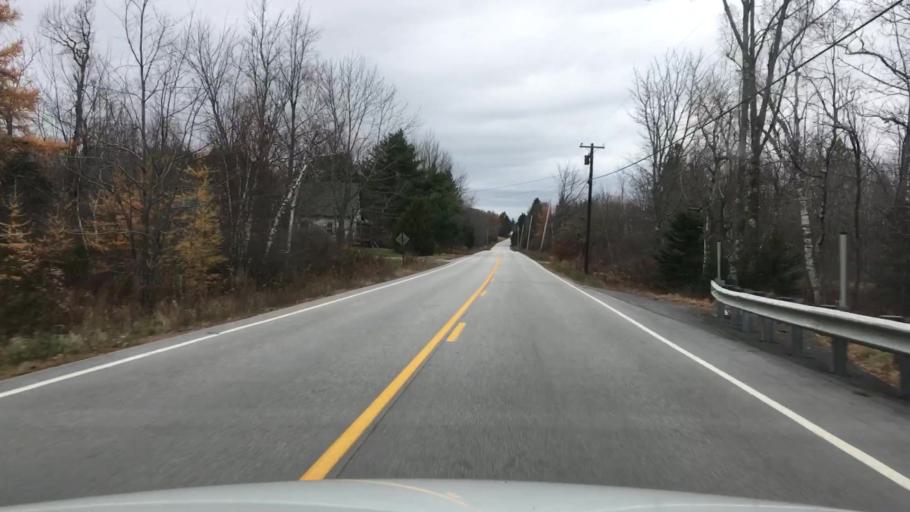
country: US
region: Maine
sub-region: Hancock County
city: Penobscot
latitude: 44.4691
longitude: -68.6361
